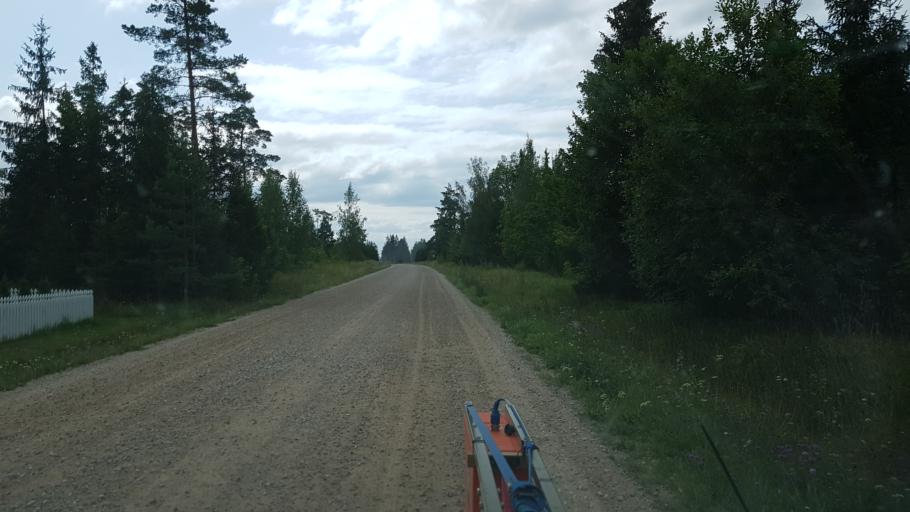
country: EE
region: Paernumaa
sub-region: Halinga vald
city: Parnu-Jaagupi
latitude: 58.5765
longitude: 24.4068
